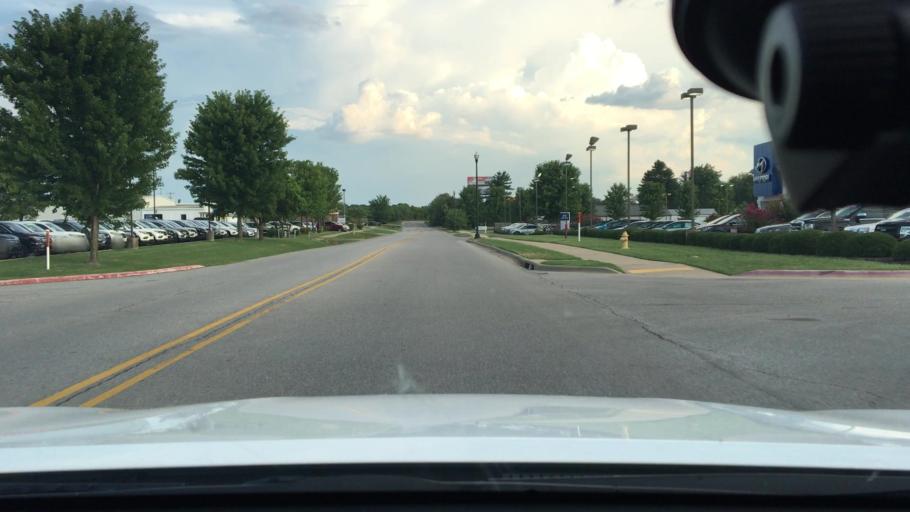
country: US
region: Arkansas
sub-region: Benton County
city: Bentonville
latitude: 36.3403
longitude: -94.1839
